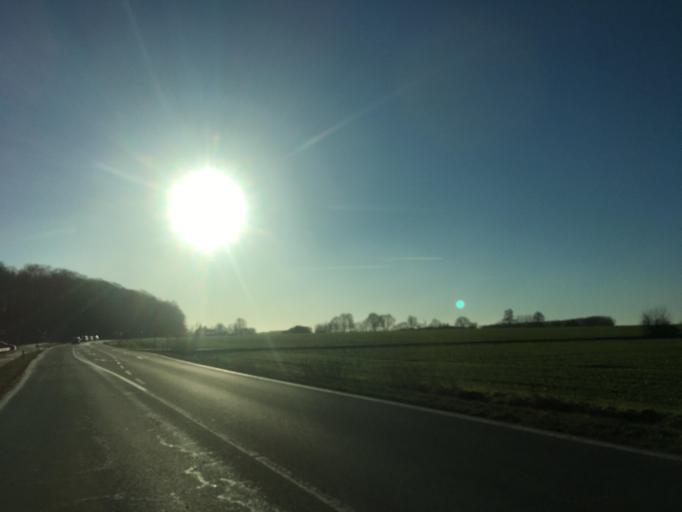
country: DE
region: North Rhine-Westphalia
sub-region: Regierungsbezirk Munster
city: Dulmen
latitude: 51.8624
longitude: 7.2857
